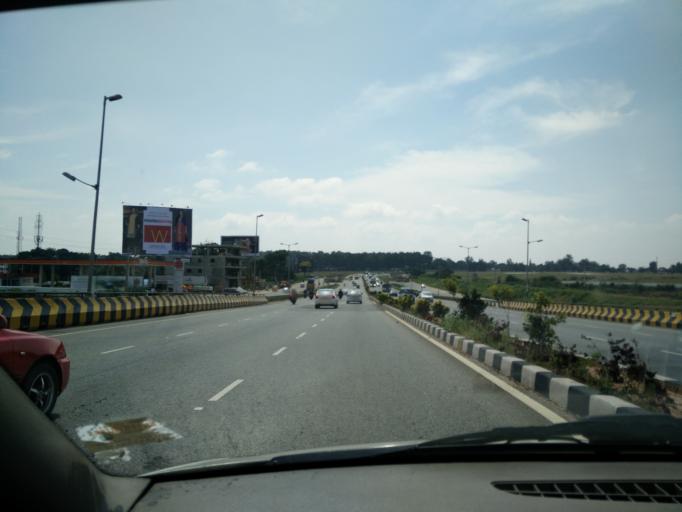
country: IN
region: Karnataka
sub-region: Bangalore Urban
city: Yelahanka
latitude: 13.1420
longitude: 77.6175
